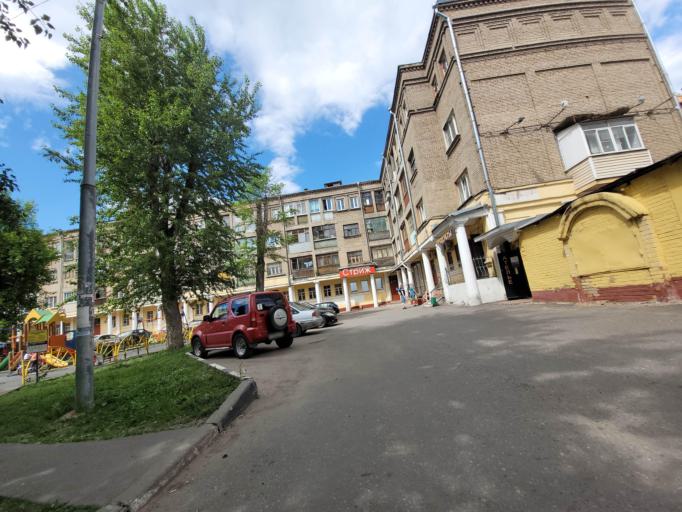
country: RU
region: Moskovskaya
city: Bolshevo
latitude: 55.9270
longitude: 37.8190
